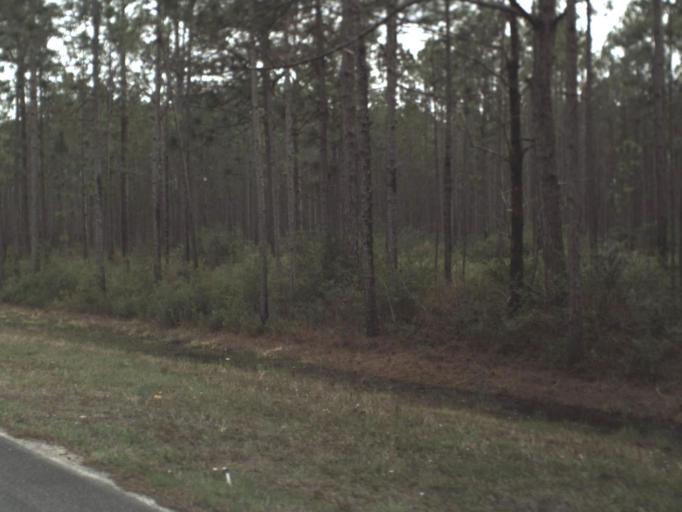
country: US
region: Florida
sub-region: Gadsden County
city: Midway
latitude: 30.3814
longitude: -84.5651
